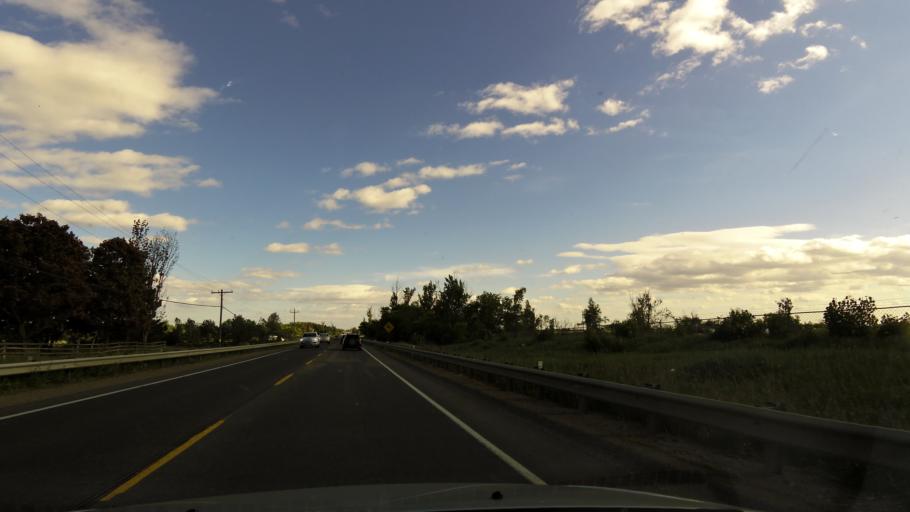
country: CA
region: Ontario
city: Vaughan
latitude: 43.8822
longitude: -79.6480
